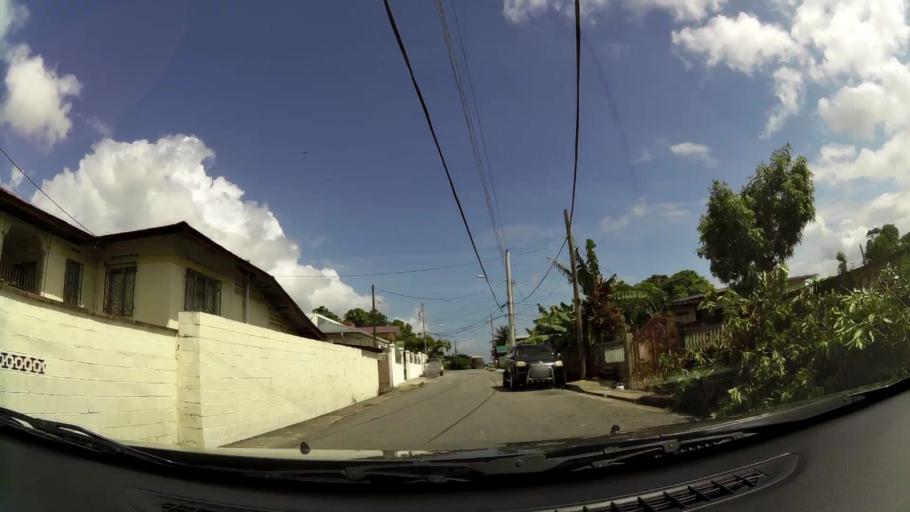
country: TT
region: Borough of Arima
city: Arima
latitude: 10.6349
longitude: -61.2762
